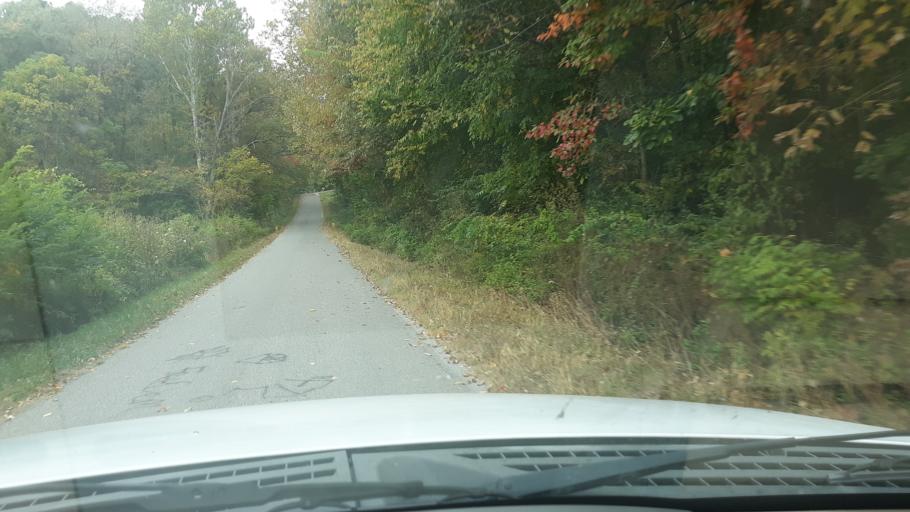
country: US
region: Illinois
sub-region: Saline County
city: Eldorado
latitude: 37.8365
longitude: -88.4942
